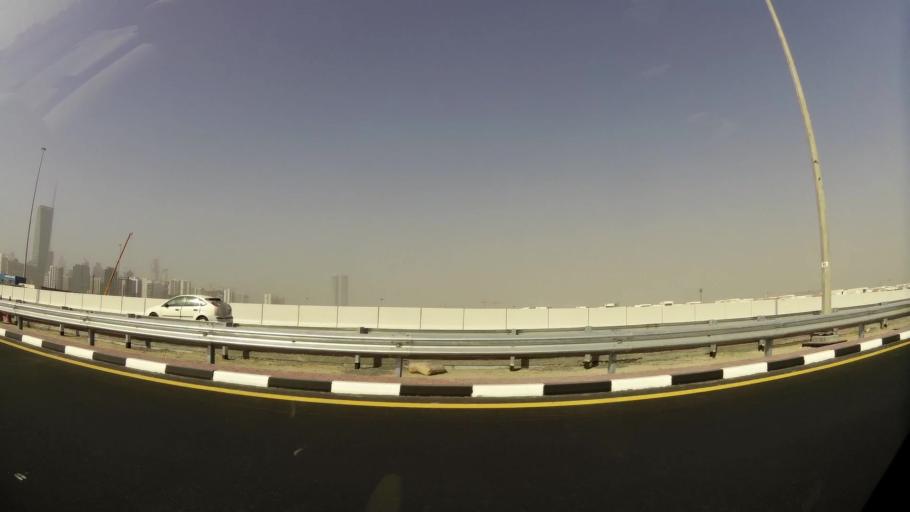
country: AE
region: Dubai
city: Dubai
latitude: 25.1675
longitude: 55.2690
